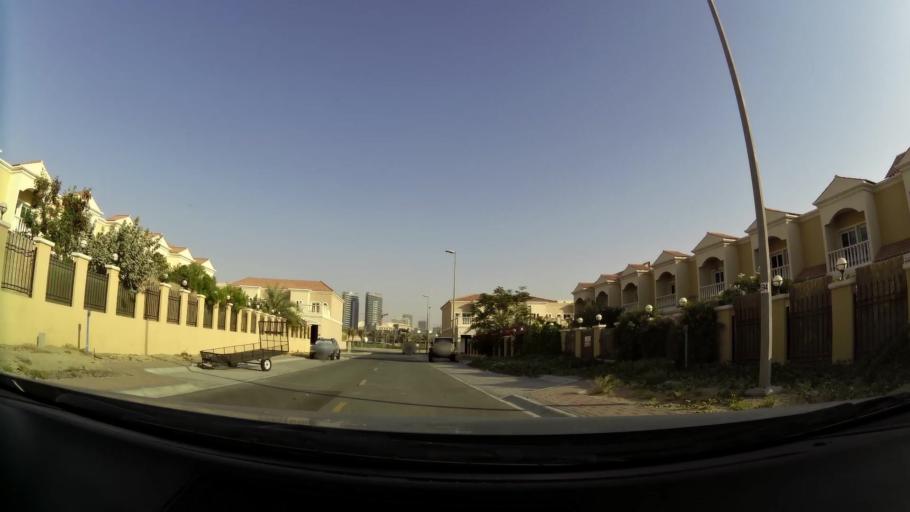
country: AE
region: Dubai
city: Dubai
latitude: 25.0568
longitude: 55.2144
